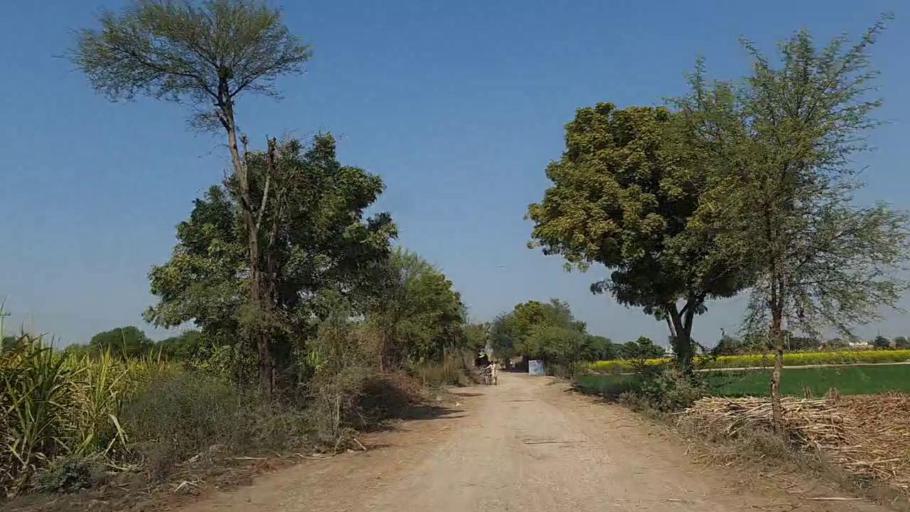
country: PK
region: Sindh
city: Daur
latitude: 26.4986
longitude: 68.2719
